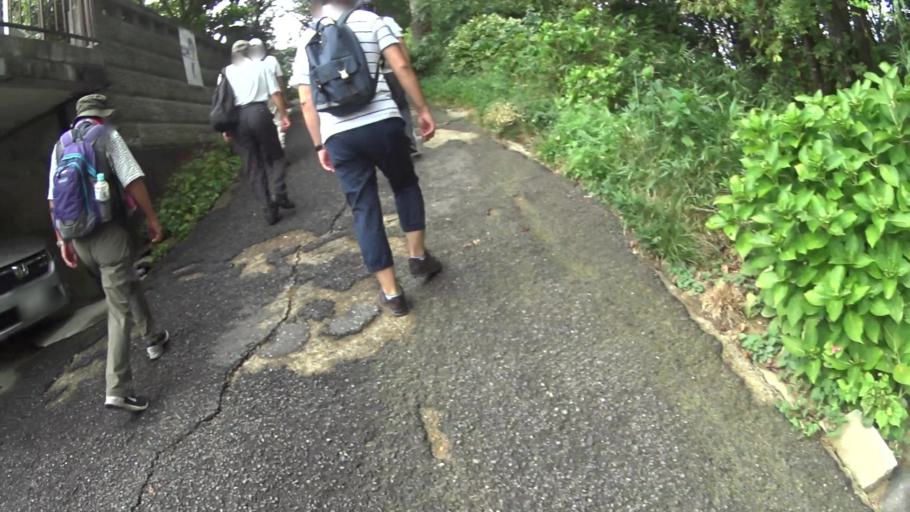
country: JP
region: Nara
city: Sakurai
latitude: 34.5062
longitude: 135.8453
